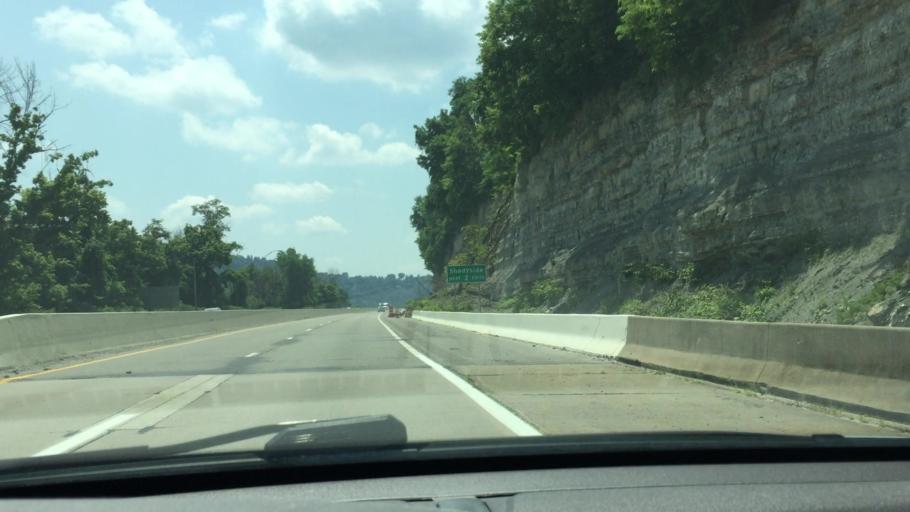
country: US
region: West Virginia
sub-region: Marshall County
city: McMechen
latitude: 39.9893
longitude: -80.7407
